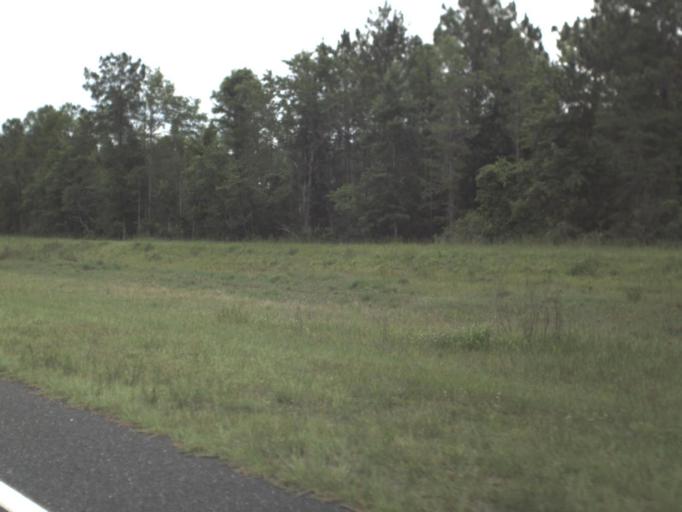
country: US
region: Florida
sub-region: Levy County
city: Chiefland
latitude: 29.3570
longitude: -82.7865
